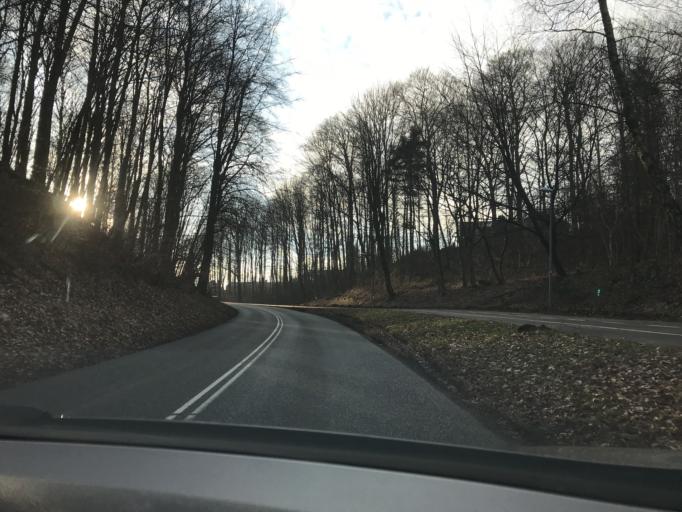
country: DK
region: South Denmark
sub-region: Vejle Kommune
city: Vejle
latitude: 55.7195
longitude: 9.5850
